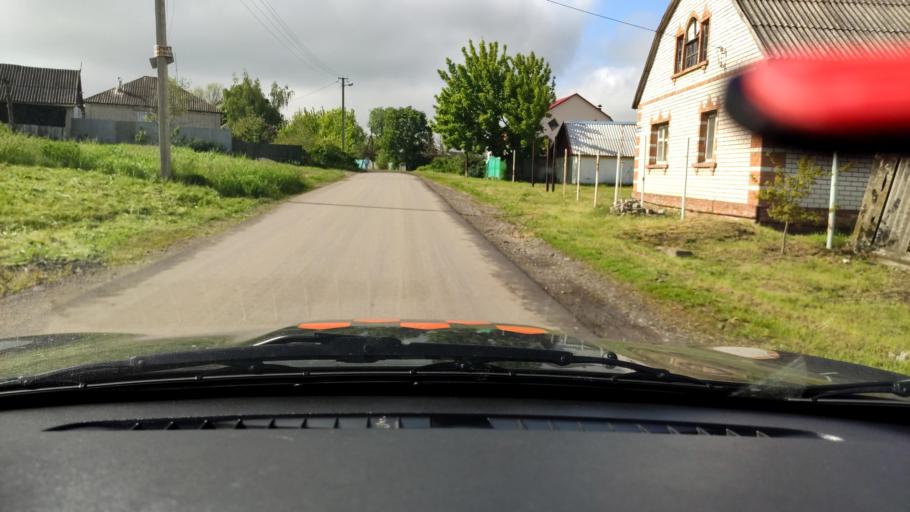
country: RU
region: Voronezj
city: Uryv-Pokrovka
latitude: 51.1083
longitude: 39.1650
